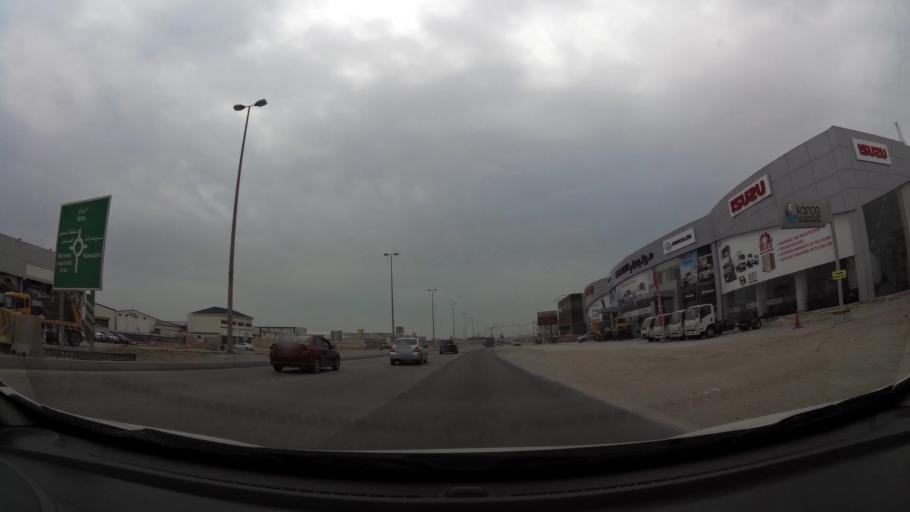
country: BH
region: Northern
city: Sitrah
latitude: 26.1344
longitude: 50.6049
